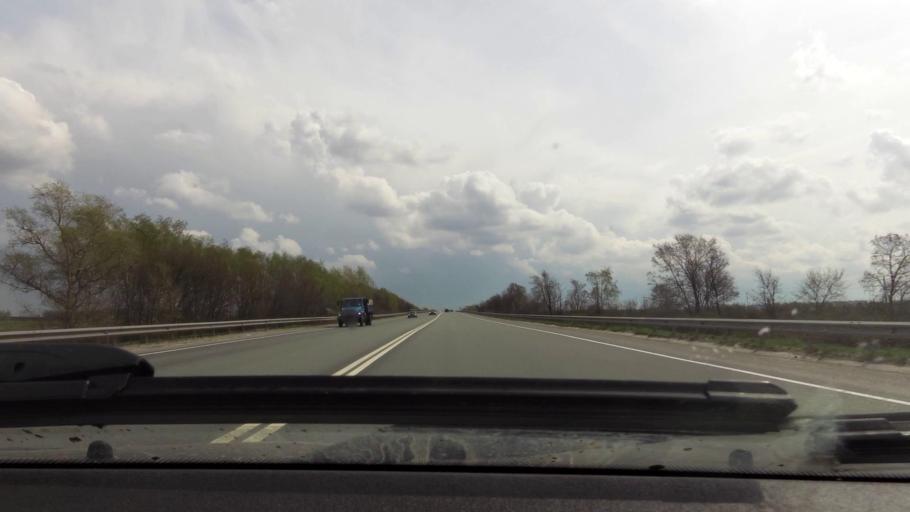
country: RU
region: Rjazan
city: Bagramovo
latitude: 54.7398
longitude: 39.4455
